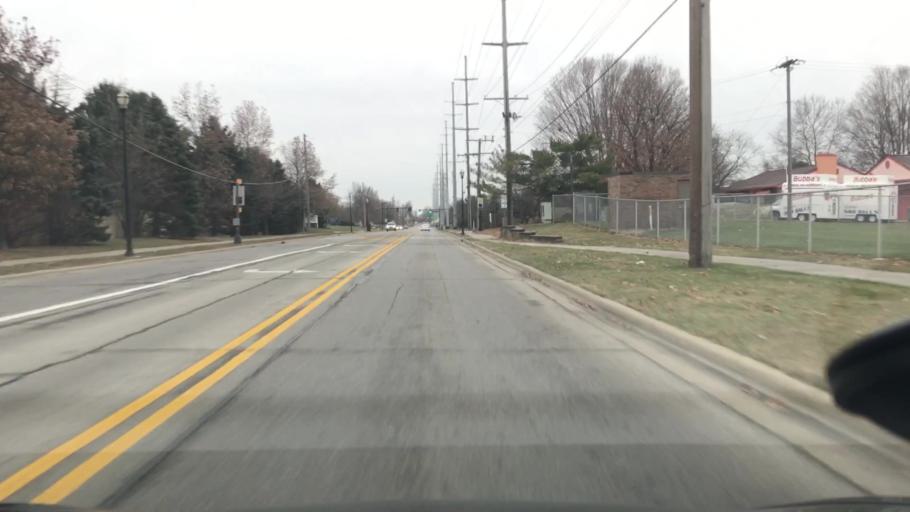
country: US
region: Ohio
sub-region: Franklin County
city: Grove City
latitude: 39.8681
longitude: -83.0706
